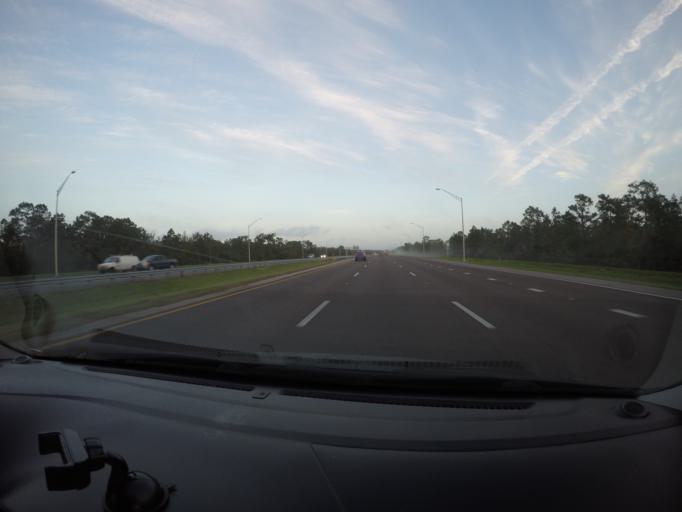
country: US
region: Florida
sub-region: Orange County
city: Azalea Park
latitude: 28.4611
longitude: -81.2325
